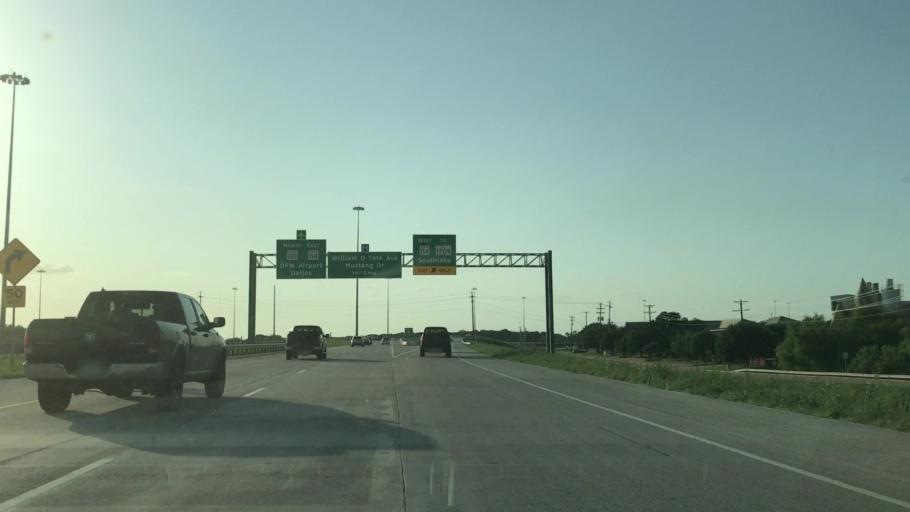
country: US
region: Texas
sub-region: Tarrant County
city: Grapevine
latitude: 32.9013
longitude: -97.0941
